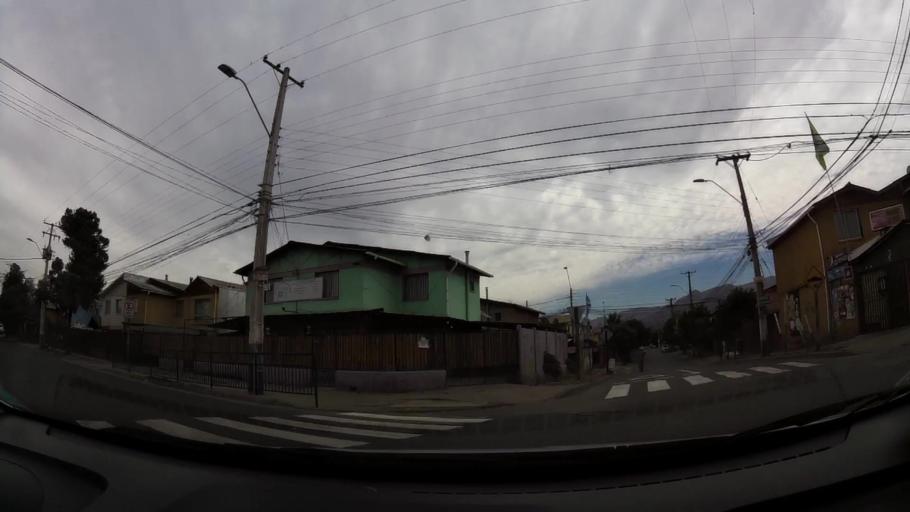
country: CL
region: O'Higgins
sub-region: Provincia de Cachapoal
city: Rancagua
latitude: -34.1243
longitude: -70.7376
